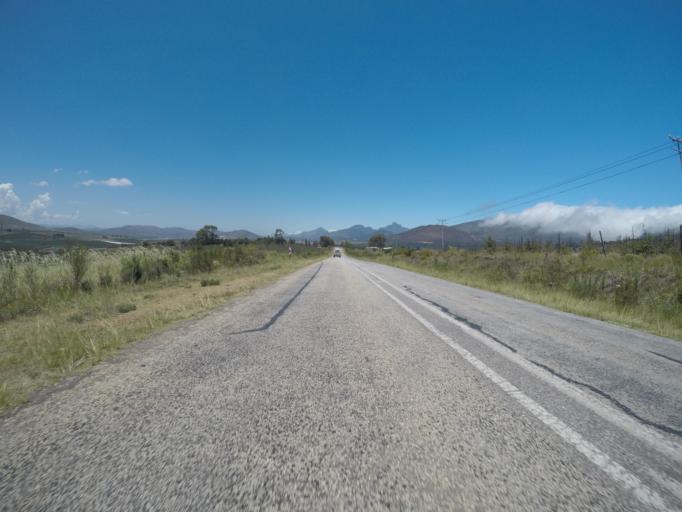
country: ZA
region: Western Cape
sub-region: Eden District Municipality
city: Plettenberg Bay
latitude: -33.7758
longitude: 23.5878
